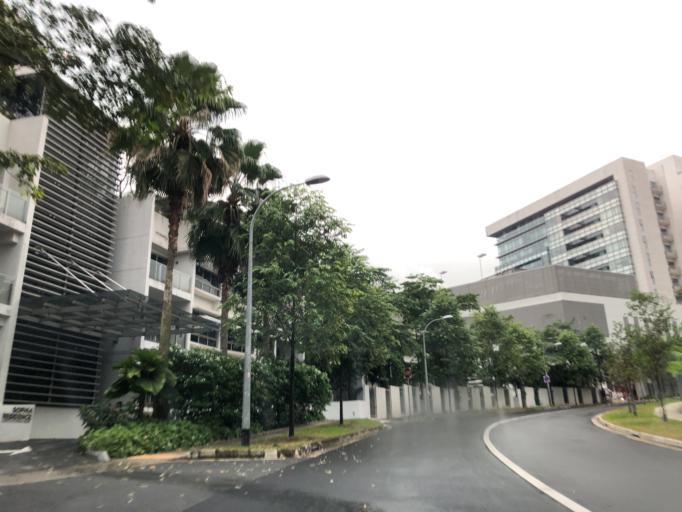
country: SG
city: Singapore
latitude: 1.3007
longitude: 103.8484
